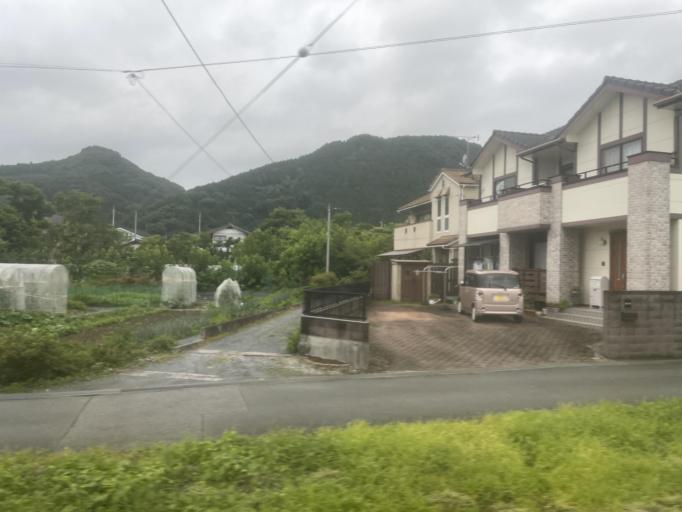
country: JP
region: Saitama
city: Kodamacho-kodamaminami
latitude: 36.1044
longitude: 139.1103
